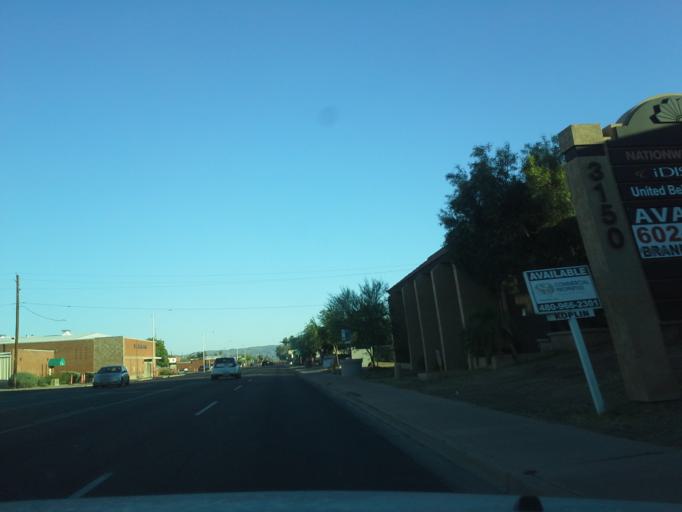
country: US
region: Arizona
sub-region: Maricopa County
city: Phoenix
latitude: 33.4853
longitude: -112.0303
